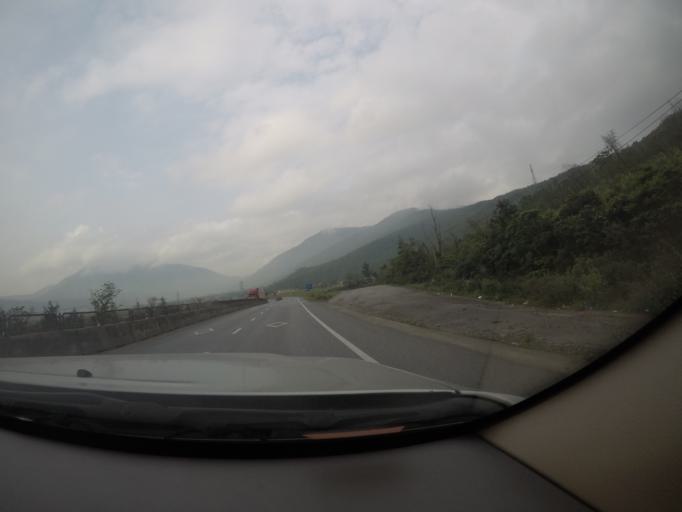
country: VN
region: Ha Tinh
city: Ky Anh
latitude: 17.9808
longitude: 106.4798
